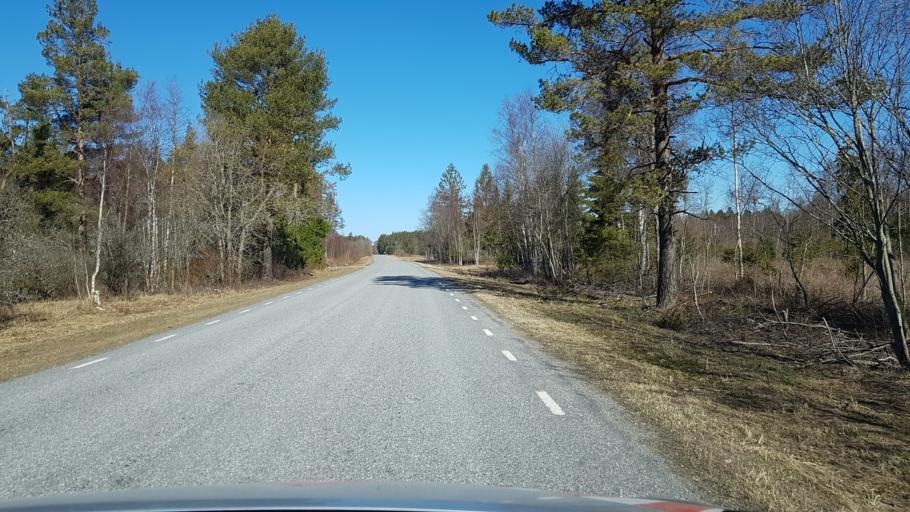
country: EE
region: Laeaene-Virumaa
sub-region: Haljala vald
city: Haljala
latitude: 59.4861
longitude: 26.2481
